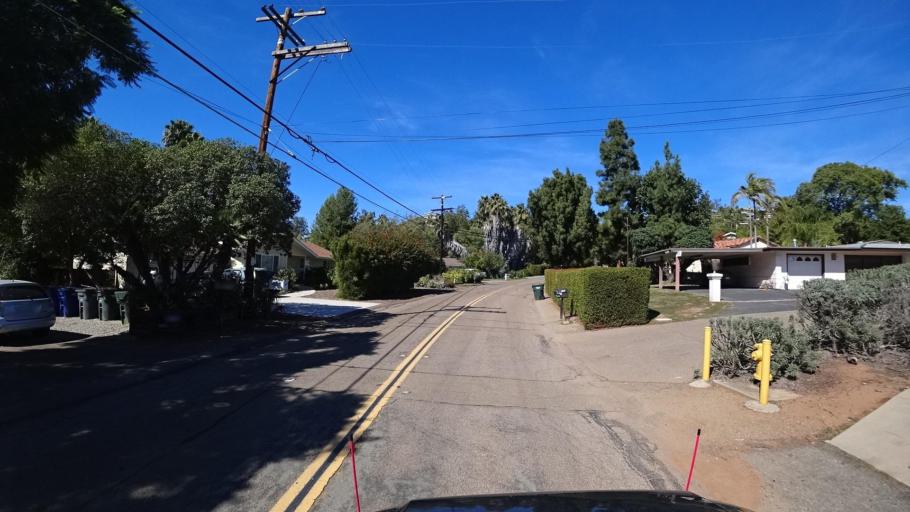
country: US
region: California
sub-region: San Diego County
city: Casa de Oro-Mount Helix
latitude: 32.7543
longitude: -116.9676
